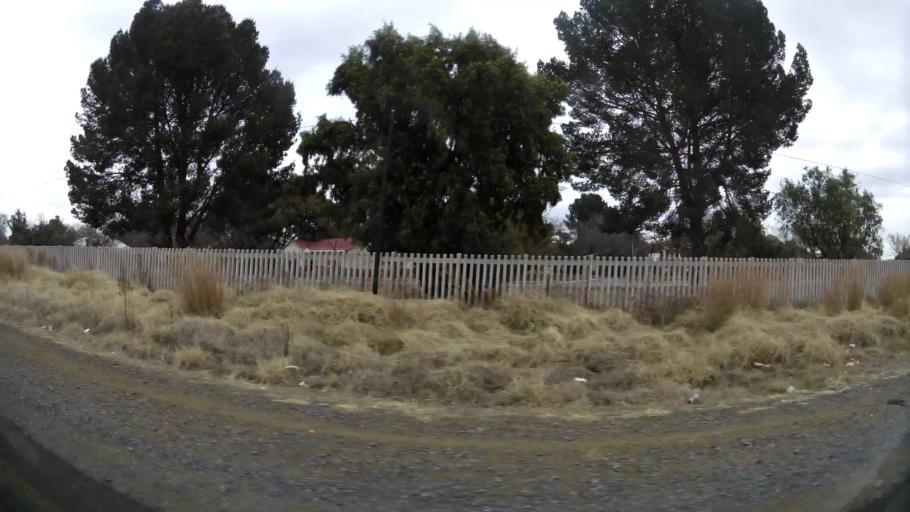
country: ZA
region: Orange Free State
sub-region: Fezile Dabi District Municipality
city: Kroonstad
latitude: -27.6299
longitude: 27.2331
